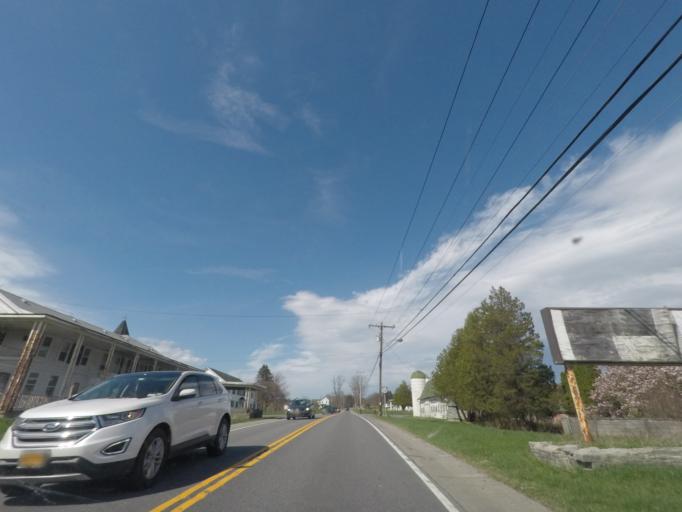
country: US
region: New York
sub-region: Greene County
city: Cairo
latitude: 42.4429
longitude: -74.0161
